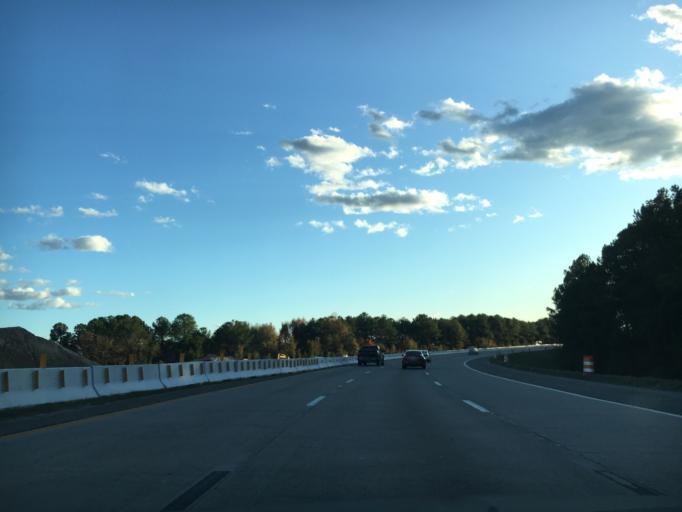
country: US
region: South Carolina
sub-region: Richland County
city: Dentsville
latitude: 34.0927
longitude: -80.9557
